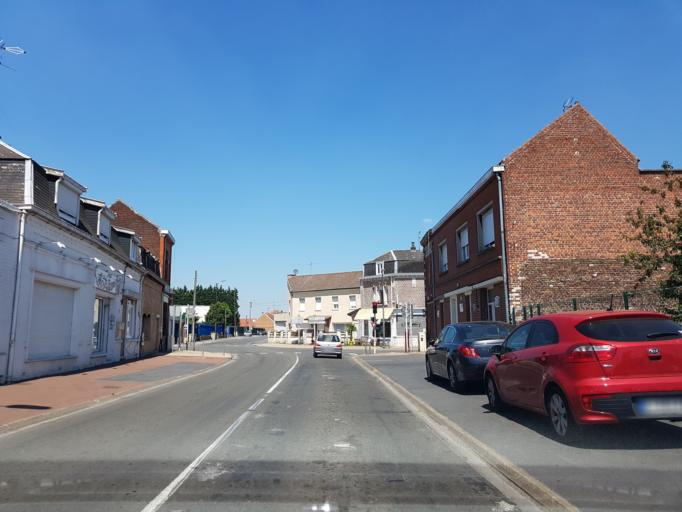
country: FR
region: Nord-Pas-de-Calais
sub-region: Departement du Nord
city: Lourches
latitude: 50.3121
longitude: 3.3451
